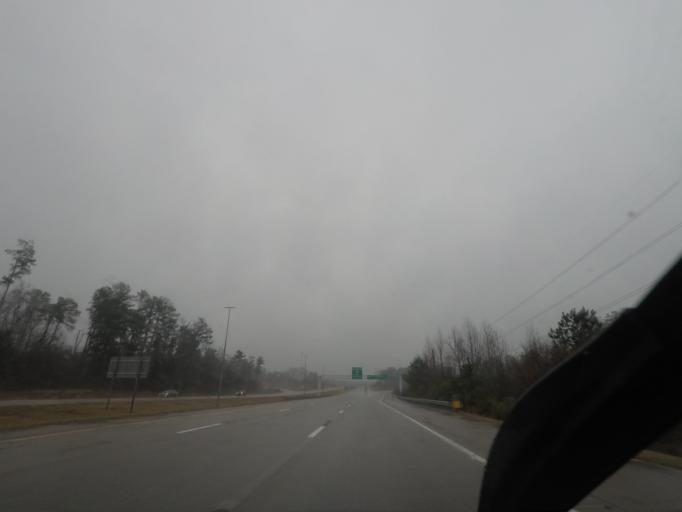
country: US
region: North Carolina
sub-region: Wake County
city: Green Level
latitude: 35.7892
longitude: -78.8881
